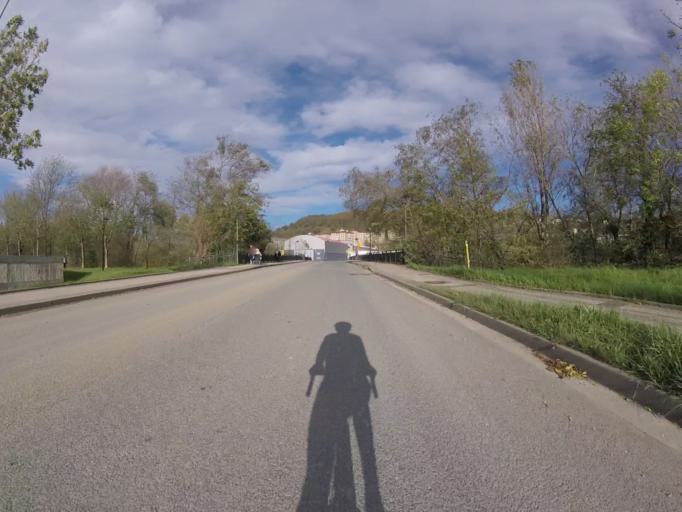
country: ES
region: Basque Country
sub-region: Provincia de Guipuzcoa
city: Hernani
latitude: 43.2699
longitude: -1.9633
